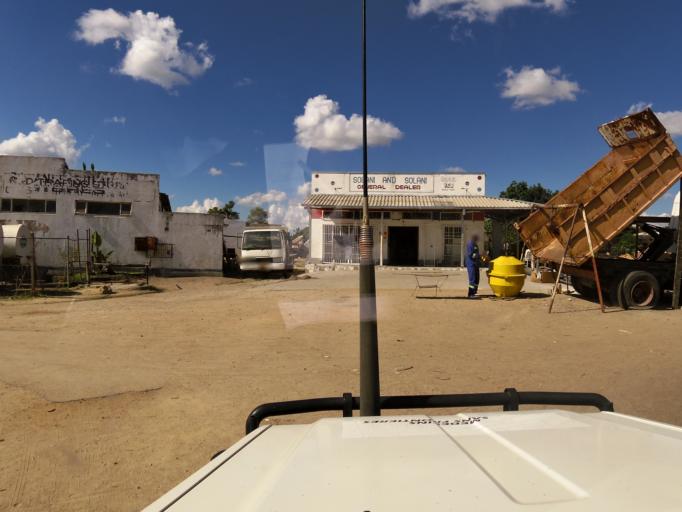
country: ZW
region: Harare
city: Epworth
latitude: -17.8767
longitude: 31.1263
